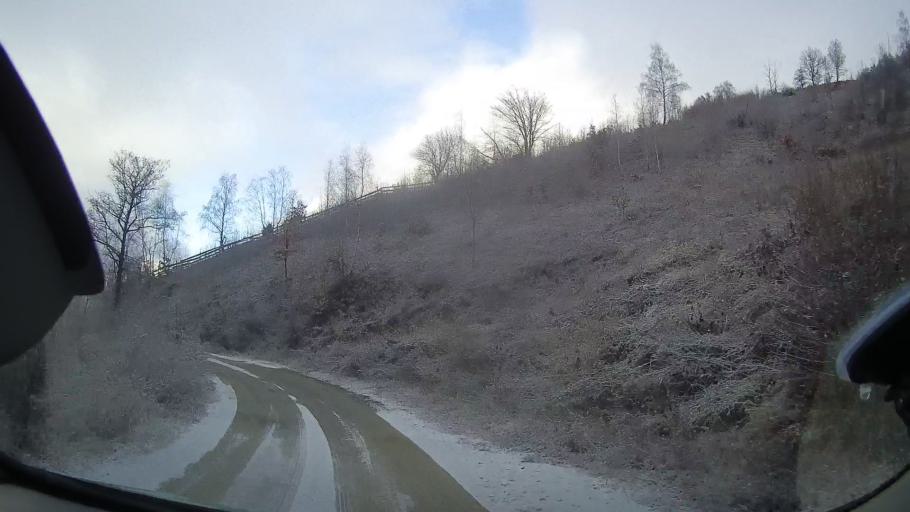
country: RO
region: Cluj
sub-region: Comuna Valea Ierii
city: Valea Ierii
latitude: 46.6695
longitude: 23.3296
